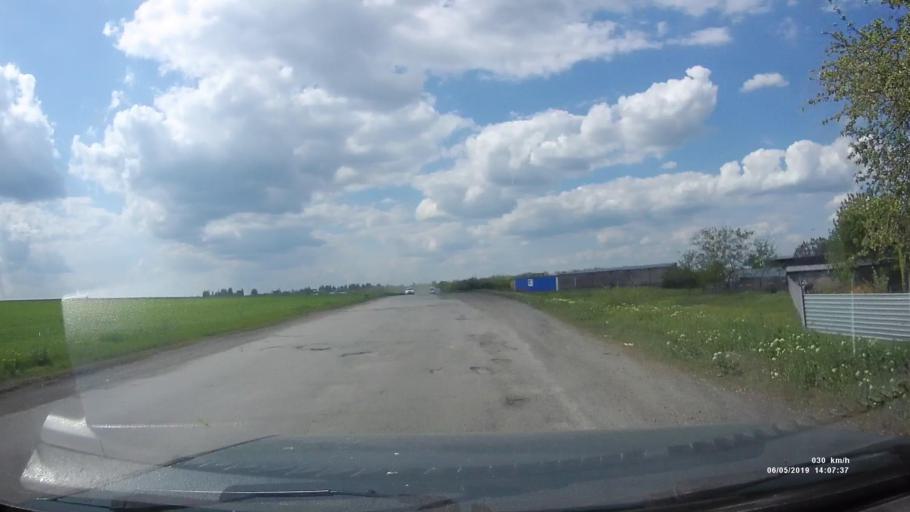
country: RU
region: Rostov
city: Shakhty
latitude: 47.6810
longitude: 40.3024
